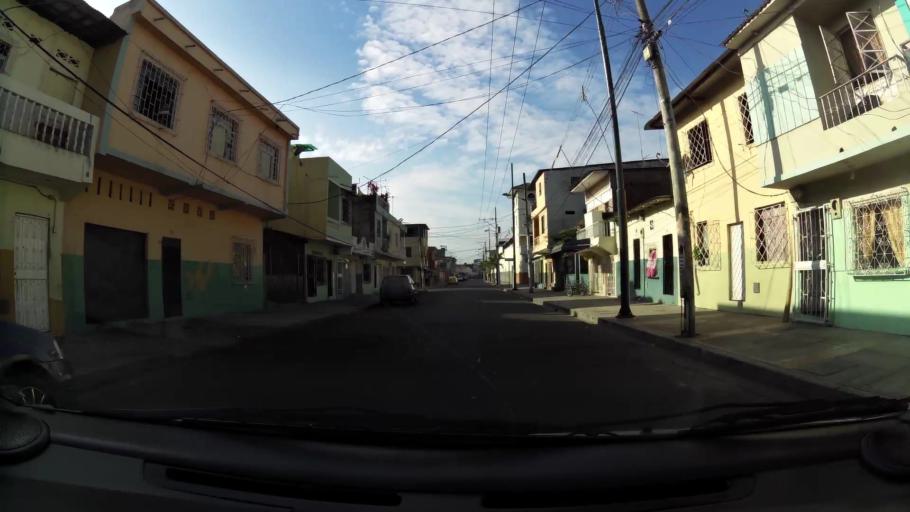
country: EC
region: Guayas
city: Guayaquil
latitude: -2.2093
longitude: -79.9077
